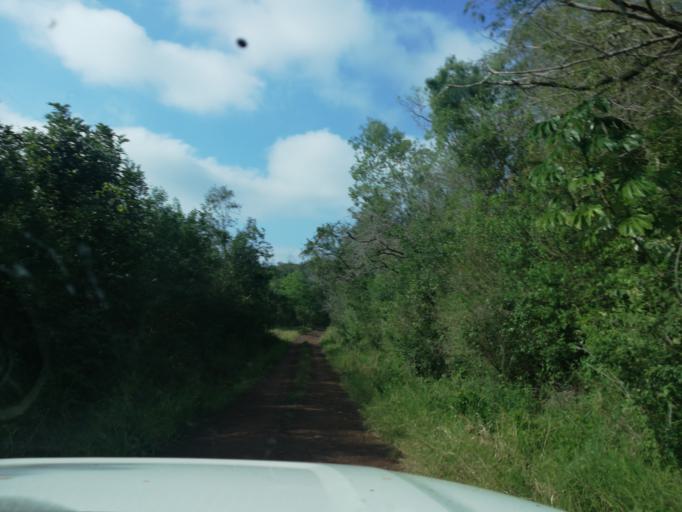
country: AR
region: Misiones
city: Cerro Azul
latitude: -27.6077
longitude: -55.5350
